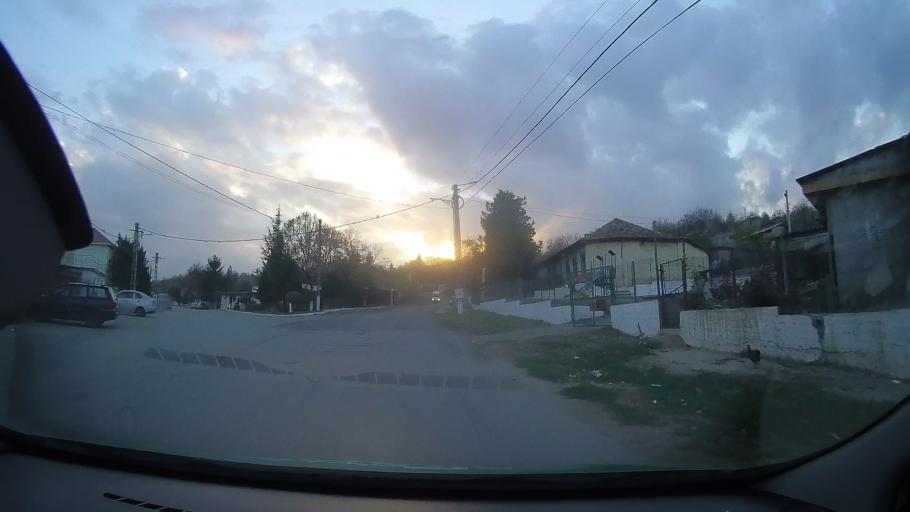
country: RO
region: Constanta
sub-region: Comuna Lipnita
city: Lipnita
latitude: 44.0934
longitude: 27.6051
